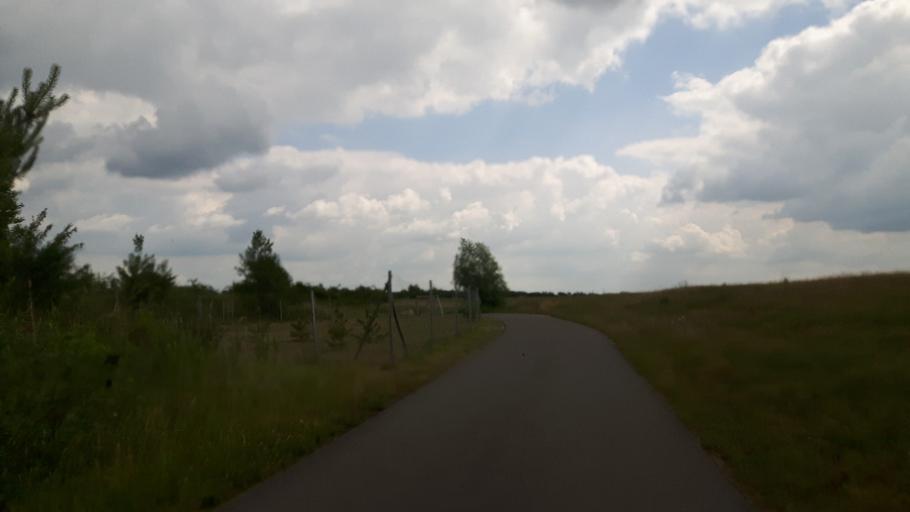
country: DE
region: Saxony-Anhalt
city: Pouch
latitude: 51.5956
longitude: 12.4164
